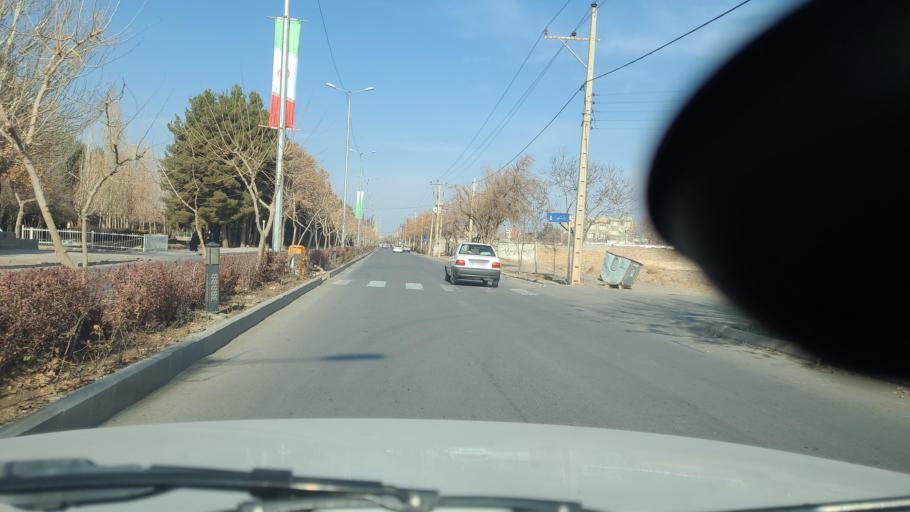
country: IR
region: Razavi Khorasan
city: Fariman
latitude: 35.6903
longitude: 59.8440
